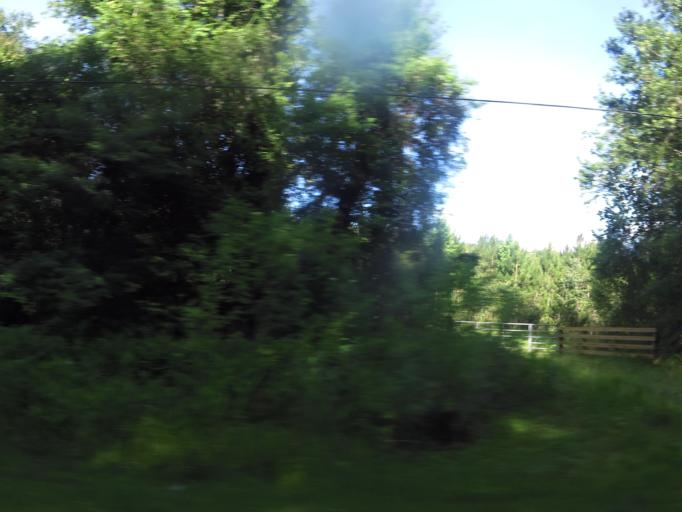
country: US
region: Florida
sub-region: Nassau County
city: Nassau Village-Ratliff
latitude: 30.4642
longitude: -81.7841
